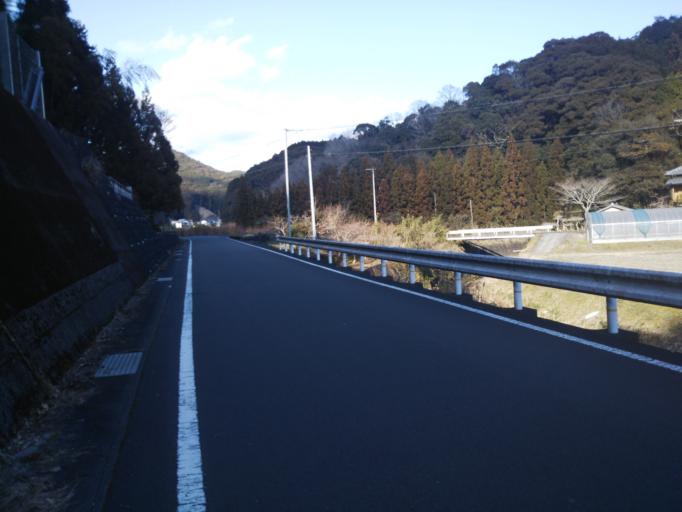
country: JP
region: Kochi
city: Nakamura
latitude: 33.0436
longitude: 132.9707
